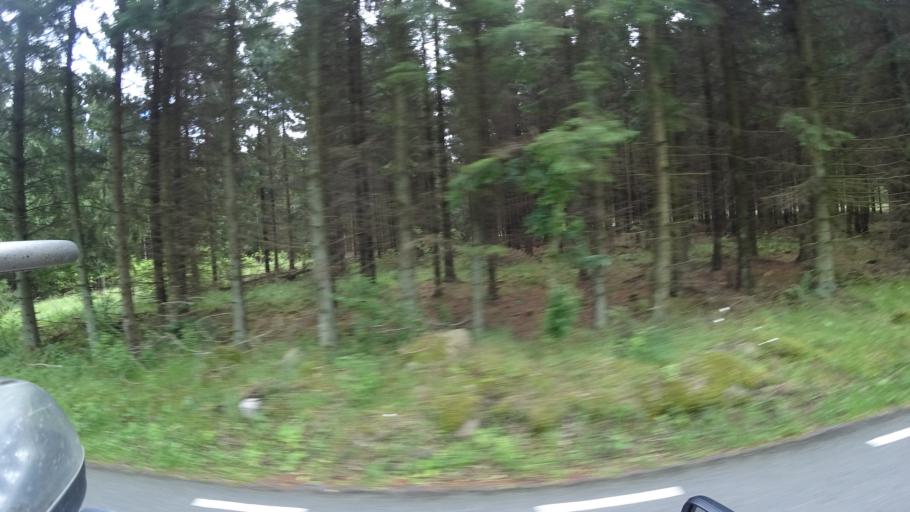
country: SE
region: Skane
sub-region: Kristianstads Kommun
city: Degeberga
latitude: 55.7222
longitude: 13.9947
